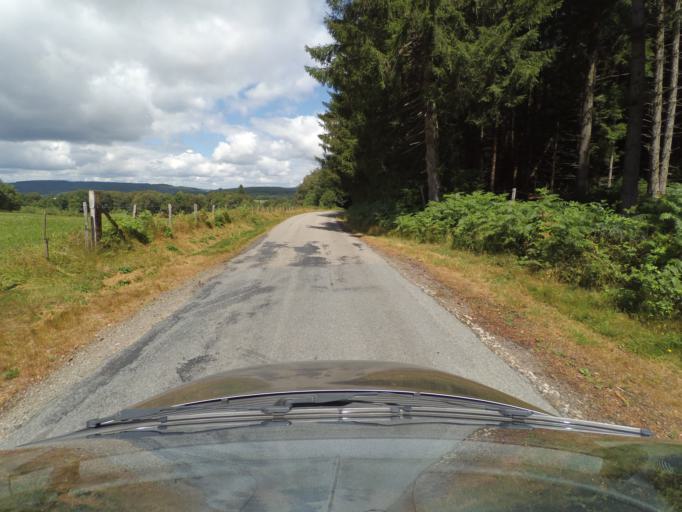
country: FR
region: Limousin
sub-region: Departement de la Creuse
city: Banize
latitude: 45.8062
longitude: 1.9325
